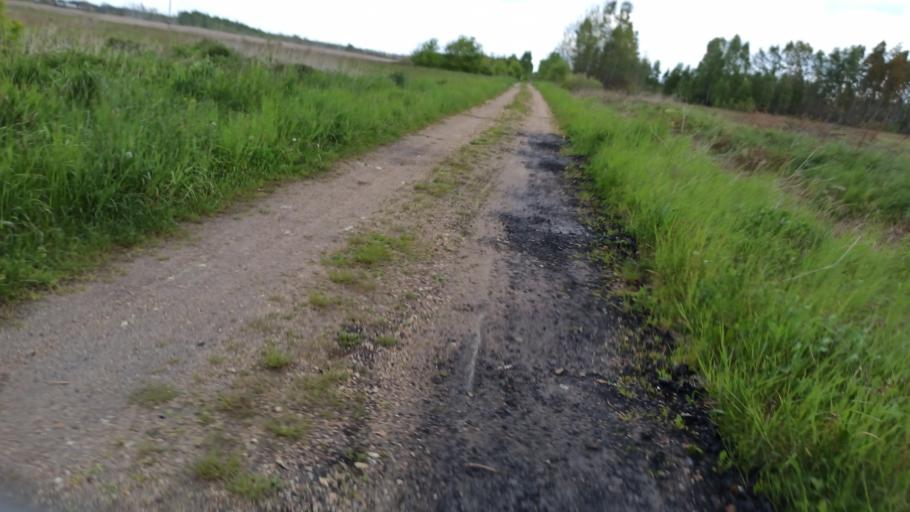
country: PL
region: Swietokrzyskie
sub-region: Powiat skarzyski
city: Skarzysko Koscielne
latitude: 51.1390
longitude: 20.9026
